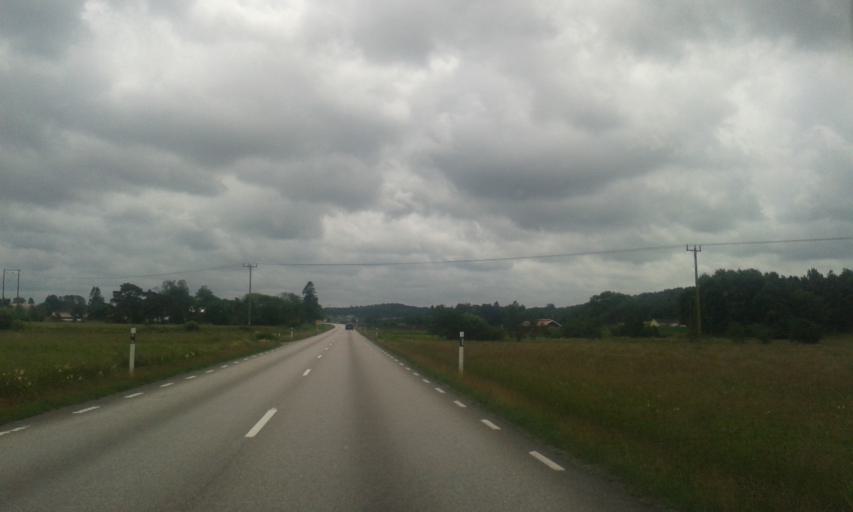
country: SE
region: Vaestra Goetaland
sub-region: Kungalvs Kommun
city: Kode
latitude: 57.8832
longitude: 11.8923
